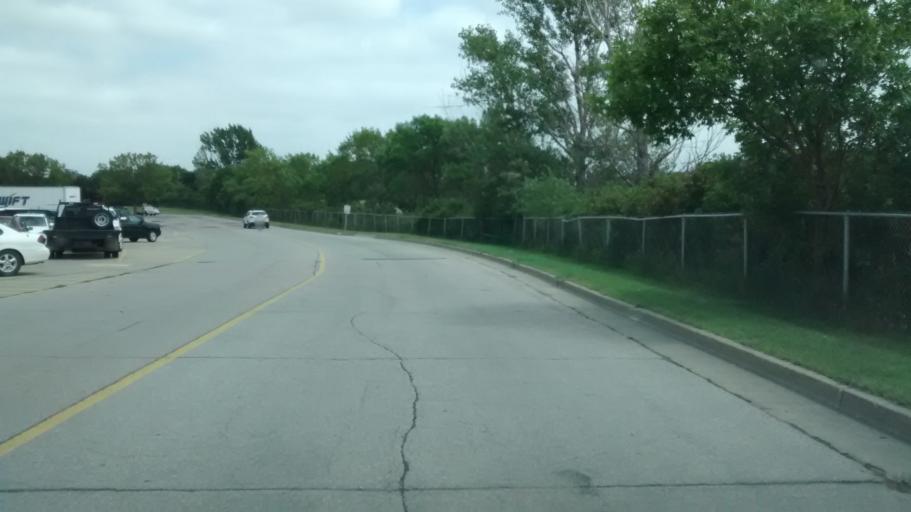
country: US
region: Iowa
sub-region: Woodbury County
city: Sergeant Bluff
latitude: 42.4443
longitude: -96.3516
